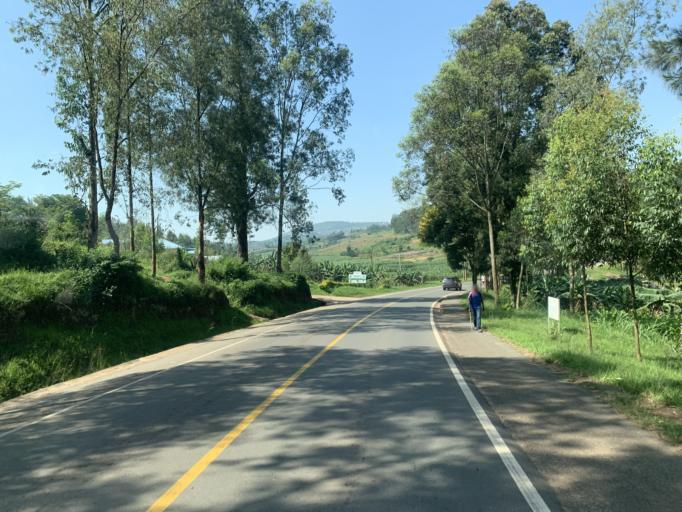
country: RW
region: Kigali
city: Kigali
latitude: -1.9895
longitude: 29.9310
